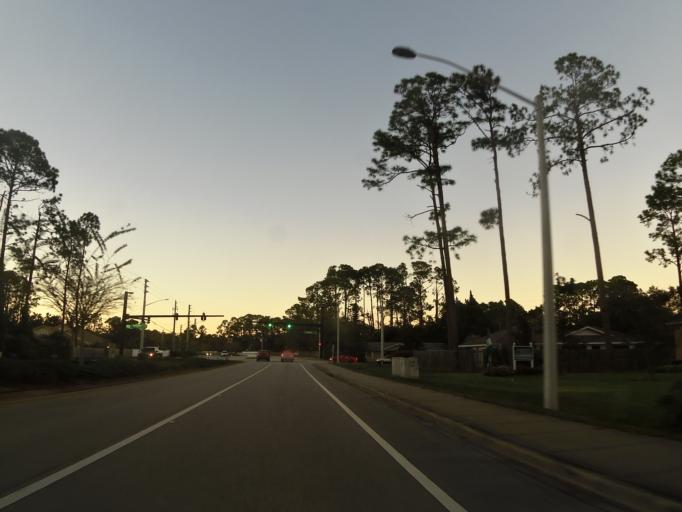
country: US
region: Florida
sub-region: Flagler County
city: Palm Coast
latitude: 29.5600
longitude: -81.2384
